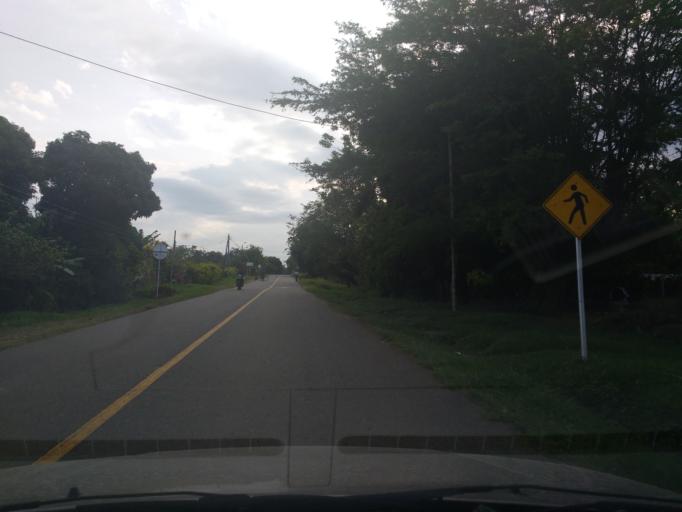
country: CO
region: Cauca
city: Caloto
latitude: 3.0920
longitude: -76.3439
